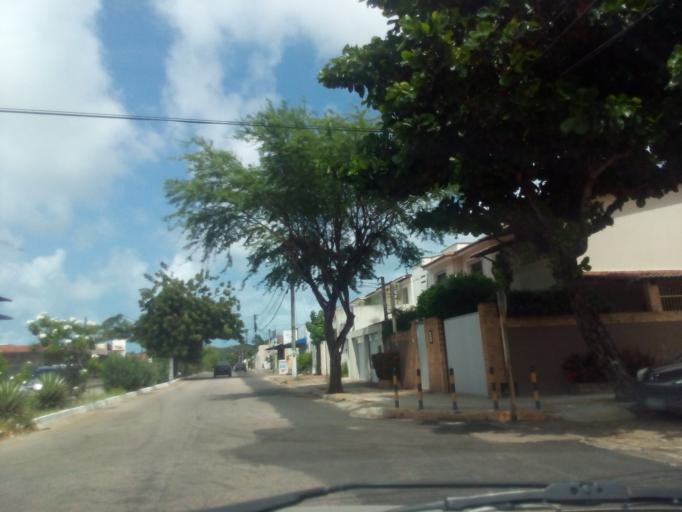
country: BR
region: Rio Grande do Norte
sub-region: Natal
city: Natal
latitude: -5.8499
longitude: -35.2030
